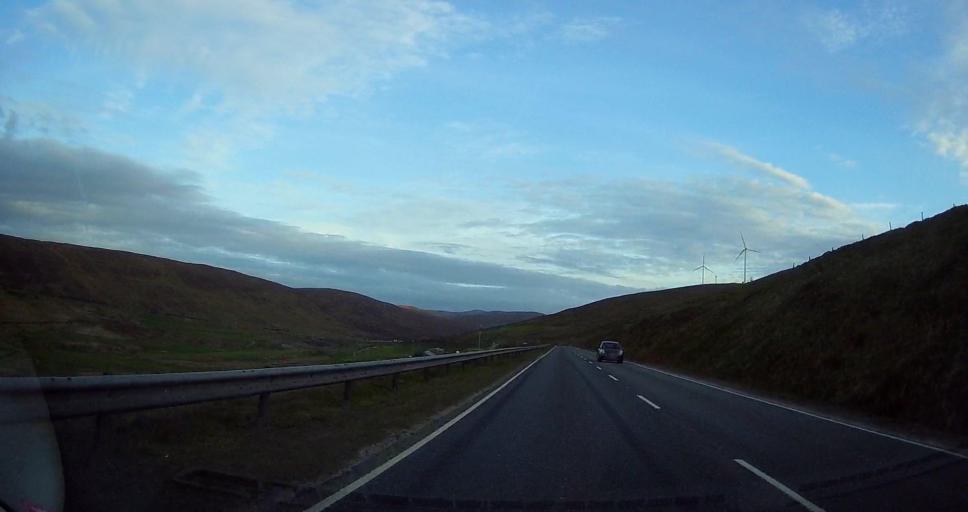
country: GB
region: Scotland
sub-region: Shetland Islands
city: Lerwick
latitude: 60.1705
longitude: -1.2255
